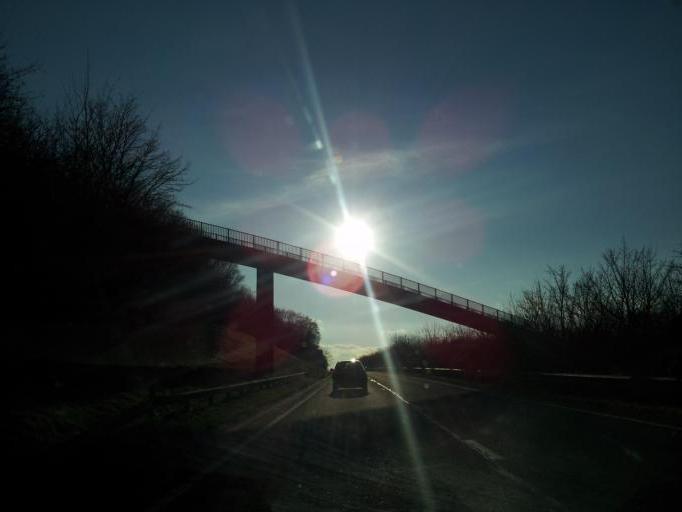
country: GB
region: England
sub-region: Devon
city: Okehampton
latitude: 50.7314
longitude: -3.9920
